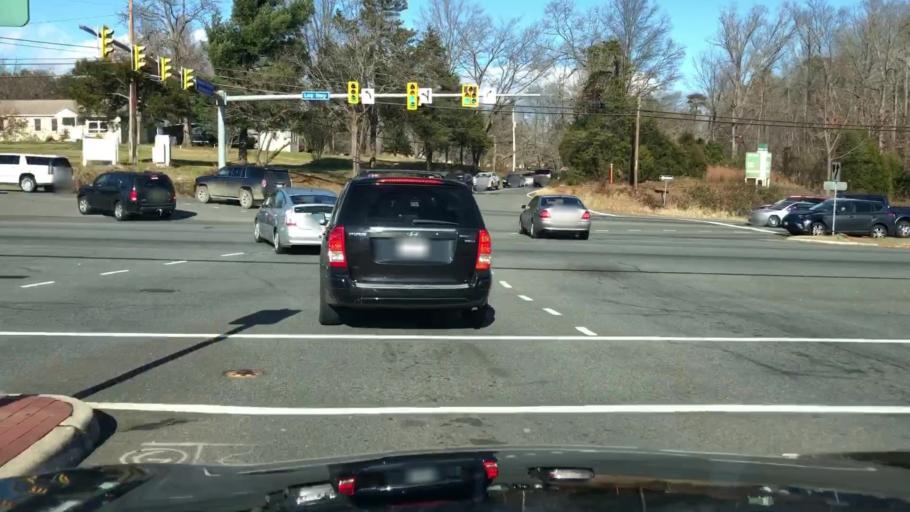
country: US
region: Virginia
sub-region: Prince William County
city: Haymarket
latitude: 38.7862
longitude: -77.6502
